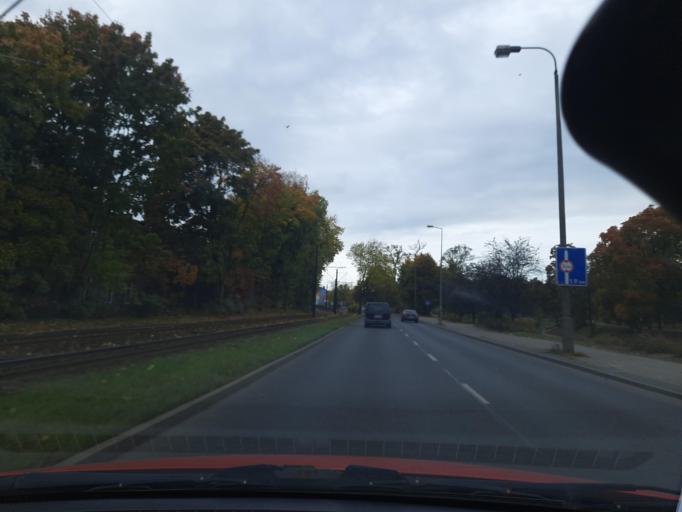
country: PL
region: Kujawsko-Pomorskie
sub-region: Bydgoszcz
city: Bydgoszcz
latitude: 53.1260
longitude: 17.9839
